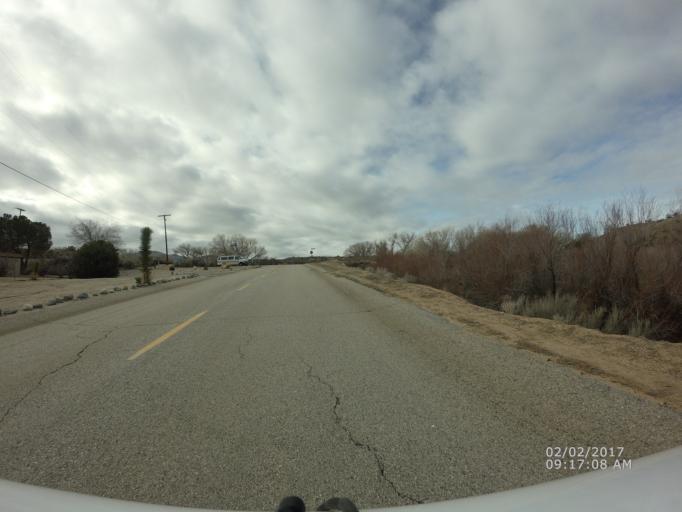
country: US
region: California
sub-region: Los Angeles County
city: Vincent
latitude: 34.5275
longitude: -118.0538
